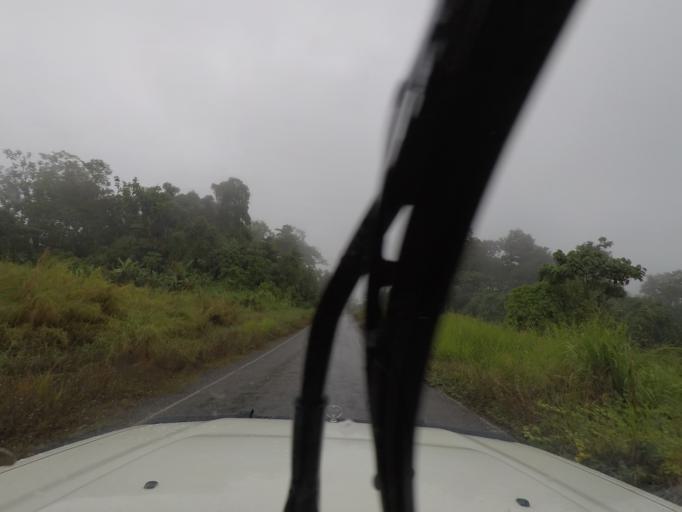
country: PG
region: Madang
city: Madang
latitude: -5.4477
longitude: 145.5151
